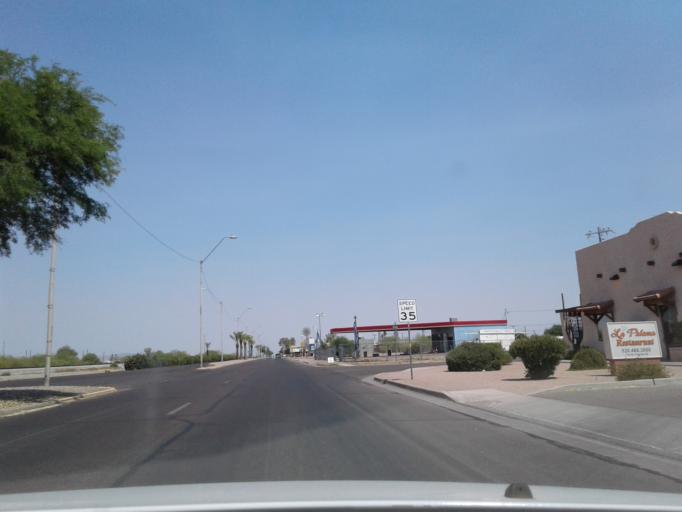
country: US
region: Arizona
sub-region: Pinal County
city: Eloy
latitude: 32.7531
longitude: -111.5566
